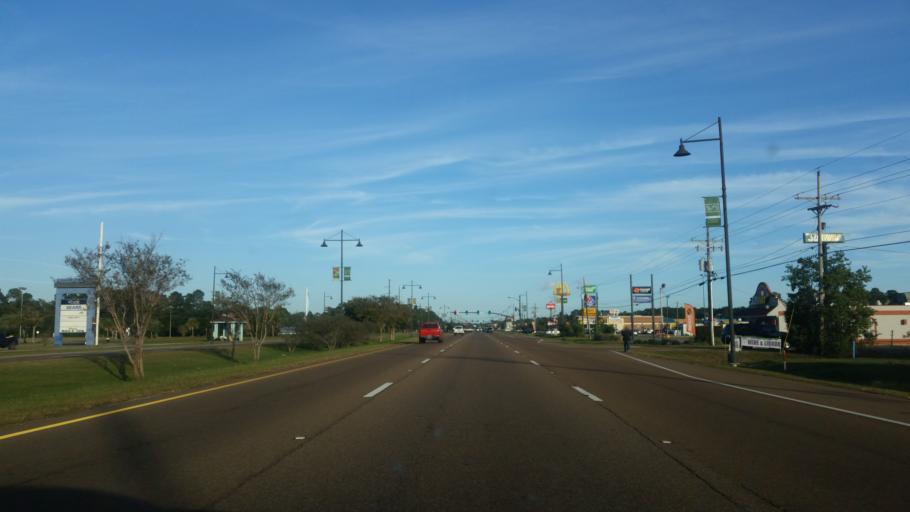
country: US
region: Mississippi
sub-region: Jackson County
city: Gautier
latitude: 30.3926
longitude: -88.6567
